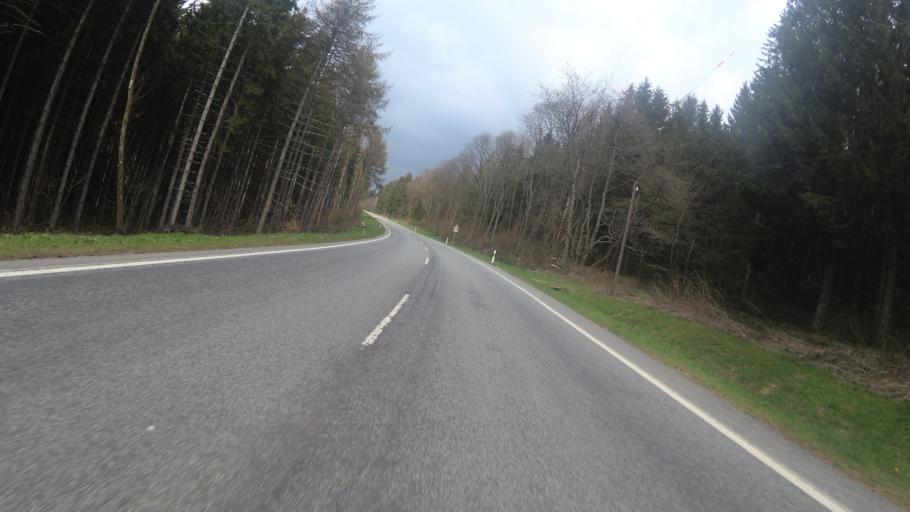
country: DE
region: Saarland
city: Nonnweiler
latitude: 49.6226
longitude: 6.9625
